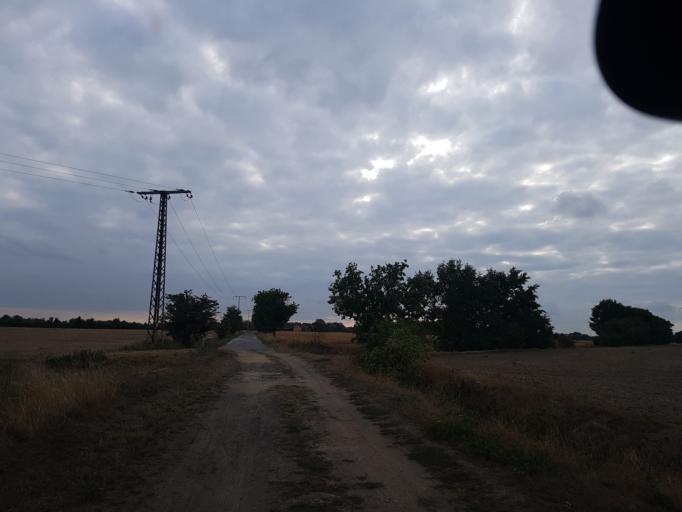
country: DE
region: Brandenburg
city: Schilda
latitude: 51.6371
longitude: 13.3297
